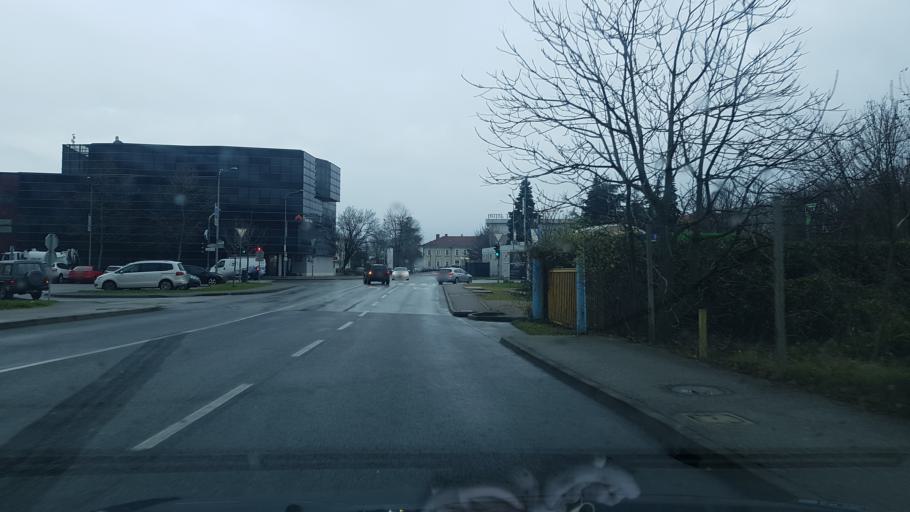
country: SI
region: Sezana
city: Sezana
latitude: 45.7065
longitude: 13.8632
